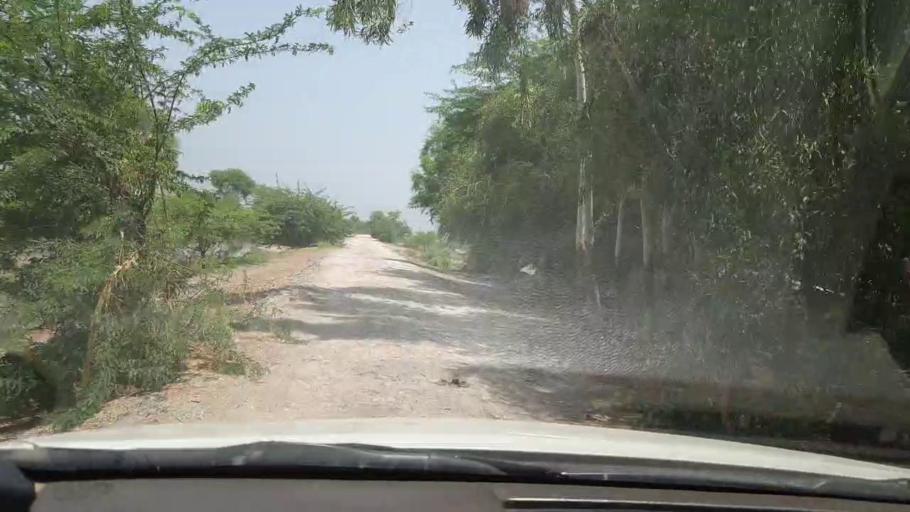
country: PK
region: Sindh
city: Garhi Yasin
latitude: 27.8954
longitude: 68.5480
